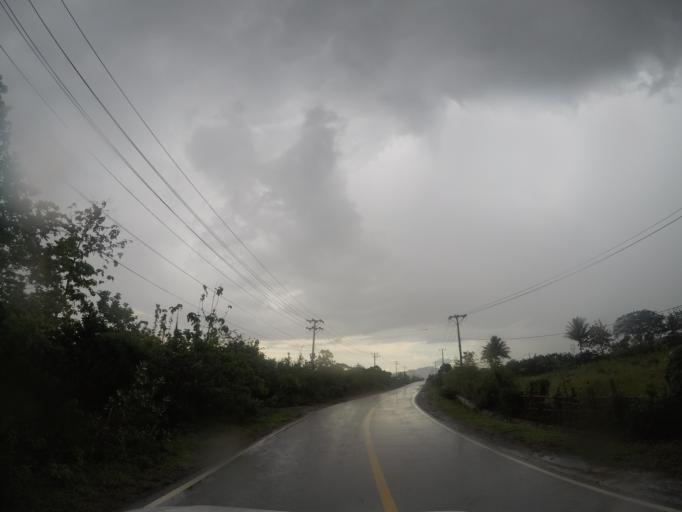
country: TL
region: Bobonaro
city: Maliana
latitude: -8.9471
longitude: 125.2054
